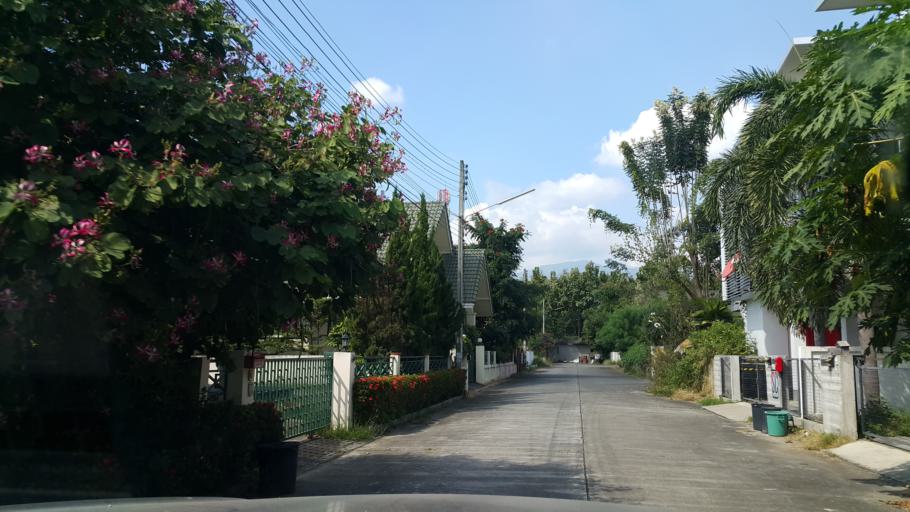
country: TH
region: Chiang Mai
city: Hang Dong
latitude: 18.7340
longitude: 98.9363
